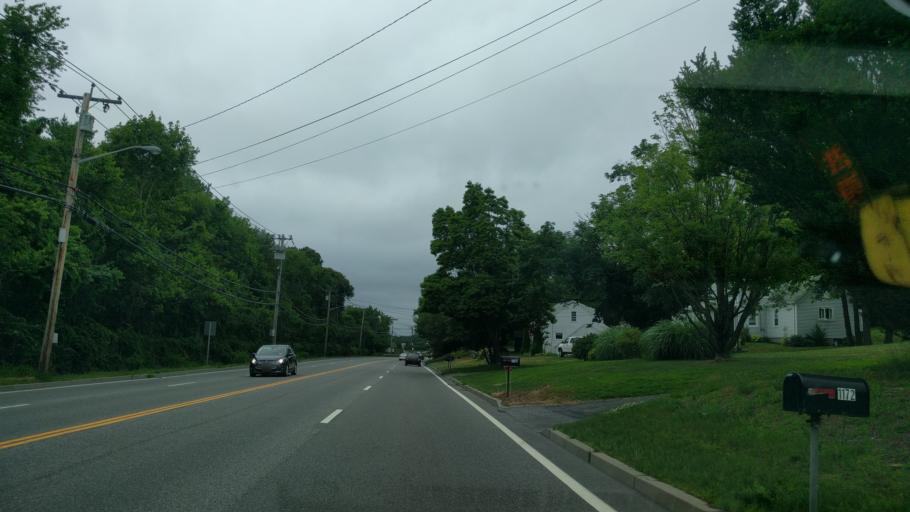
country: US
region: Rhode Island
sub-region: Newport County
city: Melville
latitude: 41.5872
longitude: -71.2687
